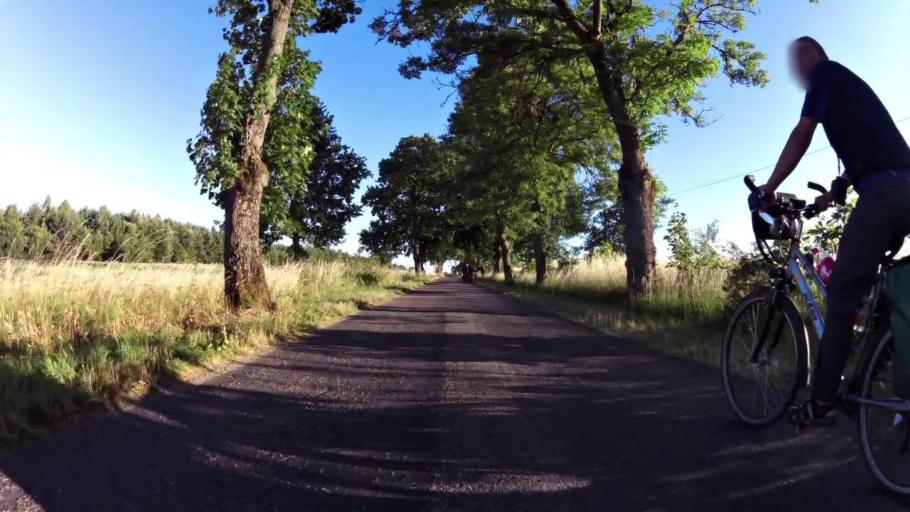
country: PL
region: West Pomeranian Voivodeship
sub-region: Powiat swidwinski
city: Swidwin
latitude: 53.7460
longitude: 15.6885
